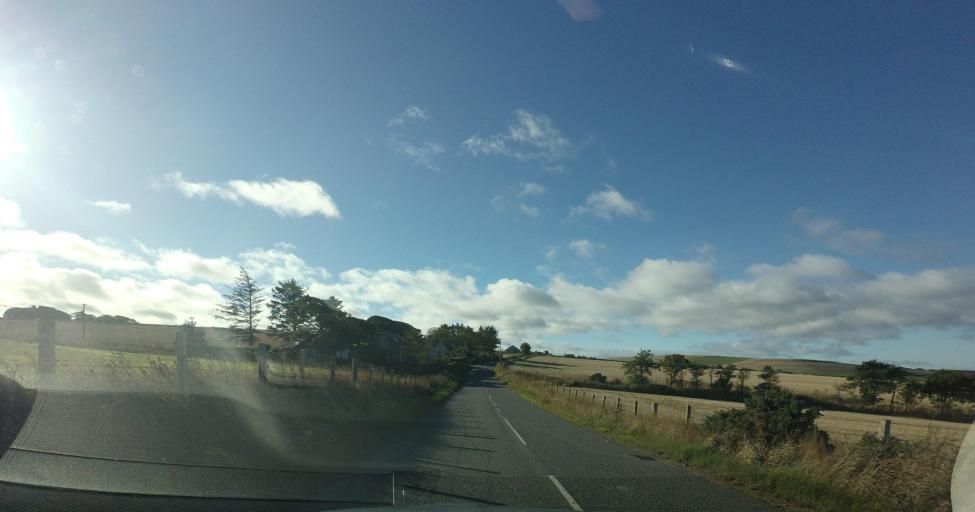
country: GB
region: Scotland
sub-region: Aberdeenshire
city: Rosehearty
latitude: 57.6696
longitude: -2.3039
